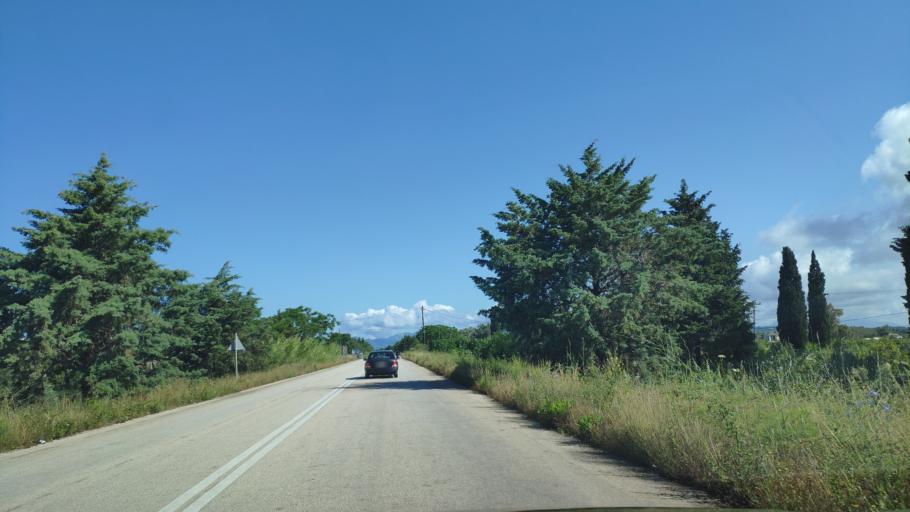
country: GR
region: Epirus
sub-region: Nomos Prevezis
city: Preveza
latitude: 38.9652
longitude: 20.7257
